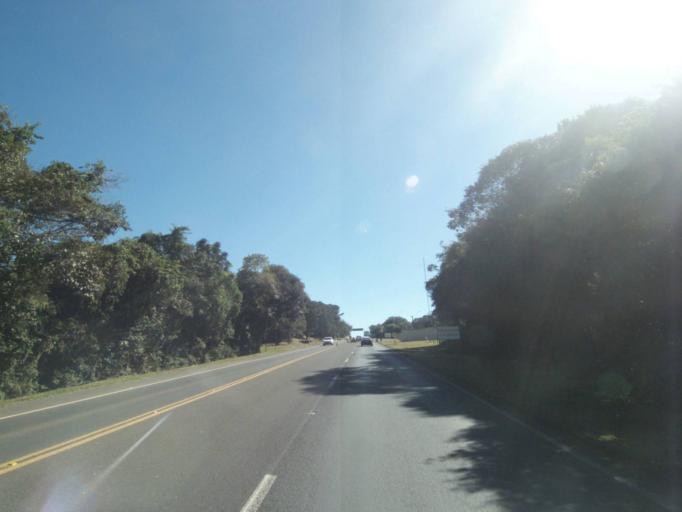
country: BR
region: Parana
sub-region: Reserva
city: Reserva
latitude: -24.6325
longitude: -50.6386
